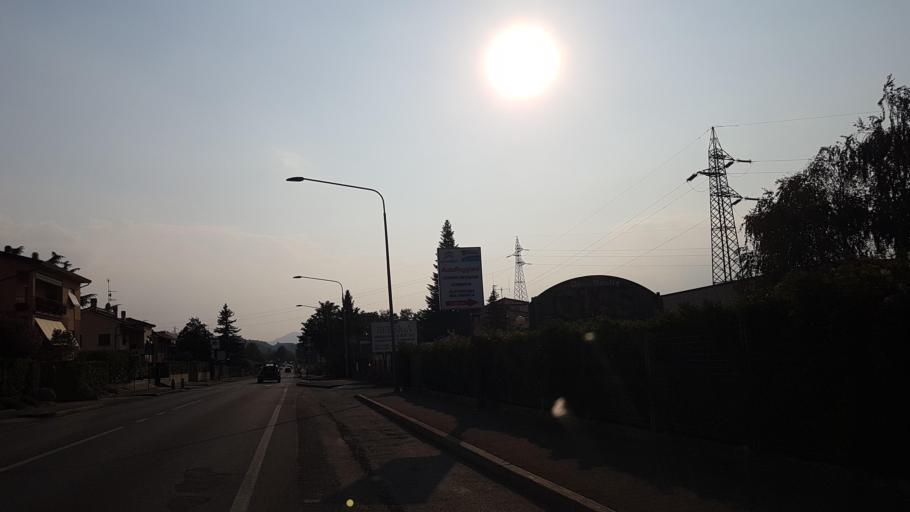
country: IT
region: Emilia-Romagna
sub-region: Provincia di Parma
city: Ozzano Taro
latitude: 44.7088
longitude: 10.1386
